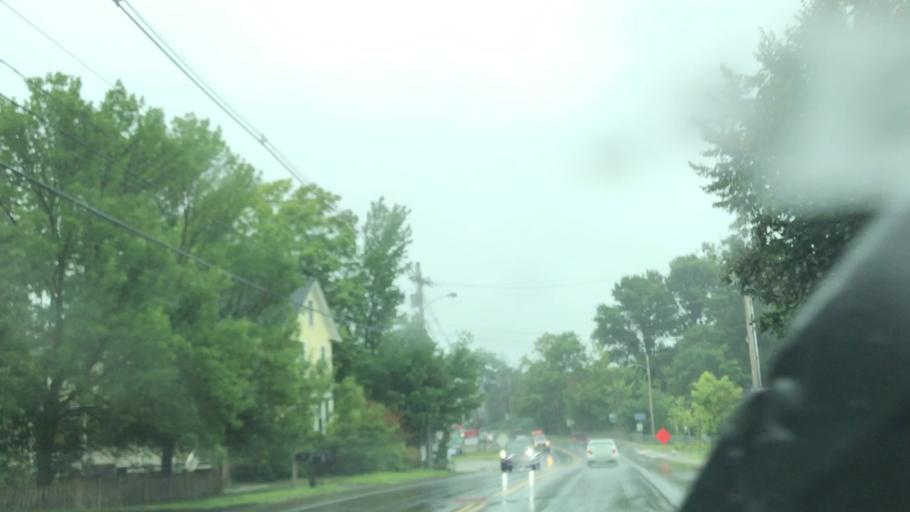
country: US
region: Maine
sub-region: York County
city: North Berwick
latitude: 43.3031
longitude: -70.7403
